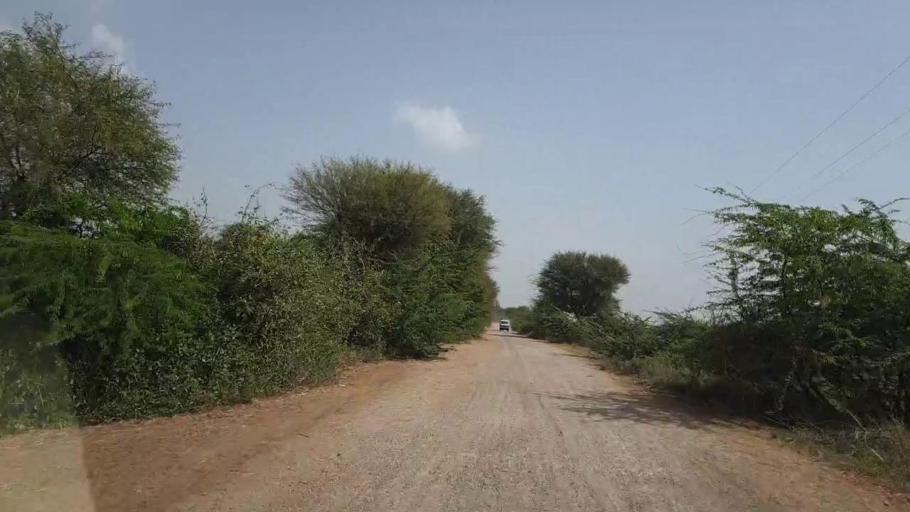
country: PK
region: Sindh
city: Rajo Khanani
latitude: 25.0519
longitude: 68.8595
